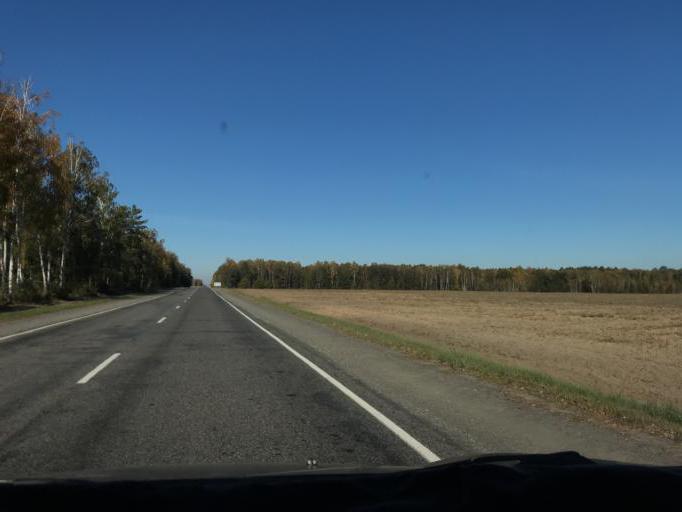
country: BY
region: Gomel
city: Yel'sk
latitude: 51.8171
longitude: 29.2093
